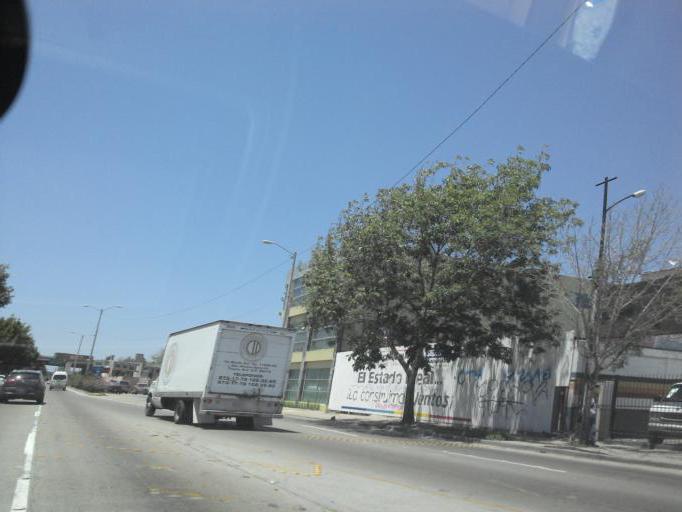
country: MX
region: Baja California
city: Tijuana
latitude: 32.5287
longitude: -117.0158
